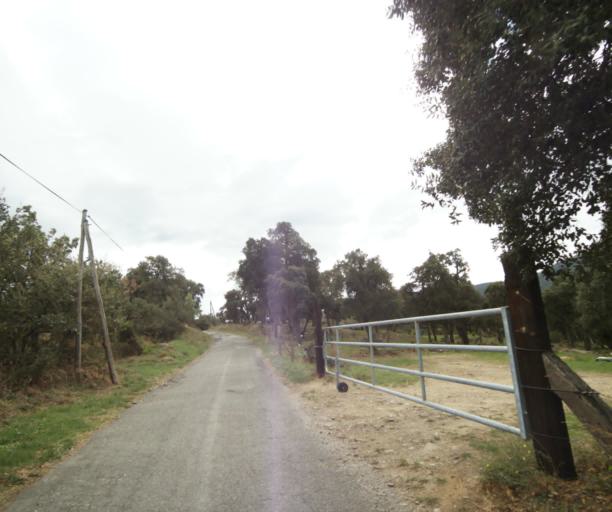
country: FR
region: Languedoc-Roussillon
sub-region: Departement des Pyrenees-Orientales
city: Collioure
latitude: 42.5272
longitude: 3.0542
